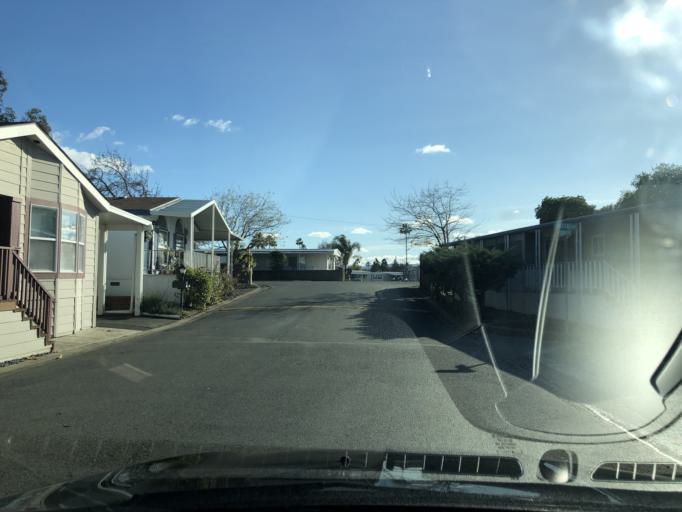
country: US
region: California
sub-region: Contra Costa County
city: Pacheco
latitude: 37.9895
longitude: -122.0650
